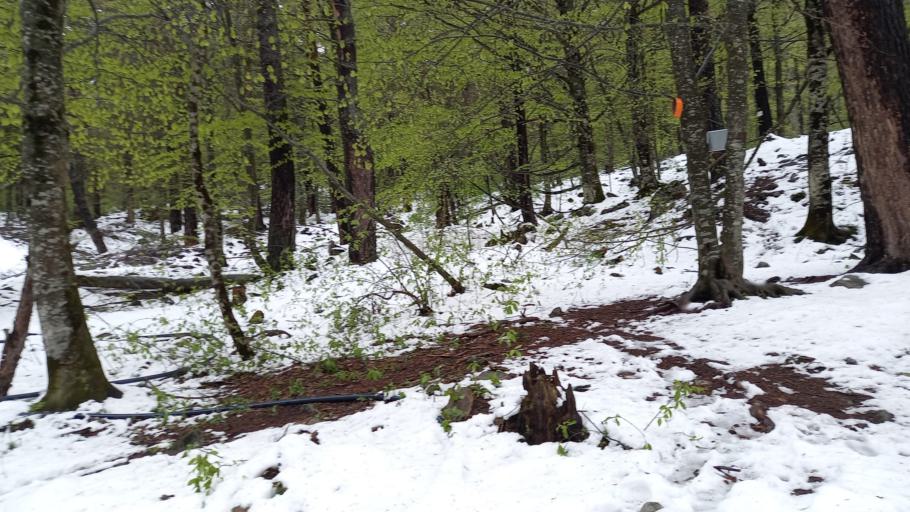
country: RU
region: North Ossetia
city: Mizur
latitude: 42.7940
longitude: 43.9222
